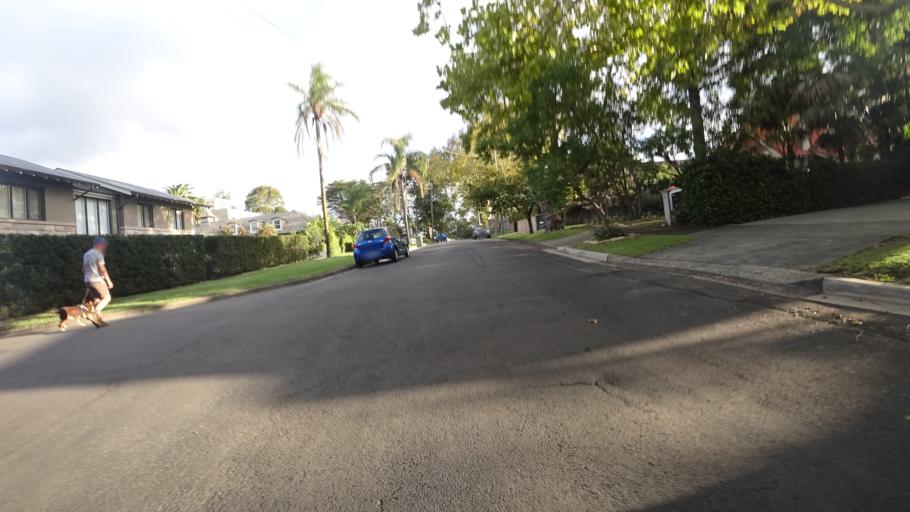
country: AU
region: New South Wales
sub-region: Lane Cove
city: Longueville
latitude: -33.8366
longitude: 151.1572
